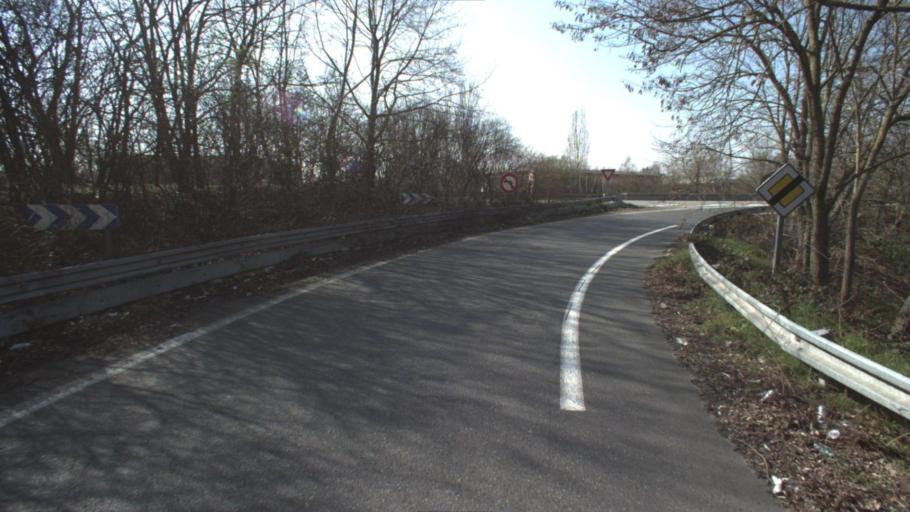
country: FR
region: Ile-de-France
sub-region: Departement de l'Essonne
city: Lisses
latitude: 48.6124
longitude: 2.4305
